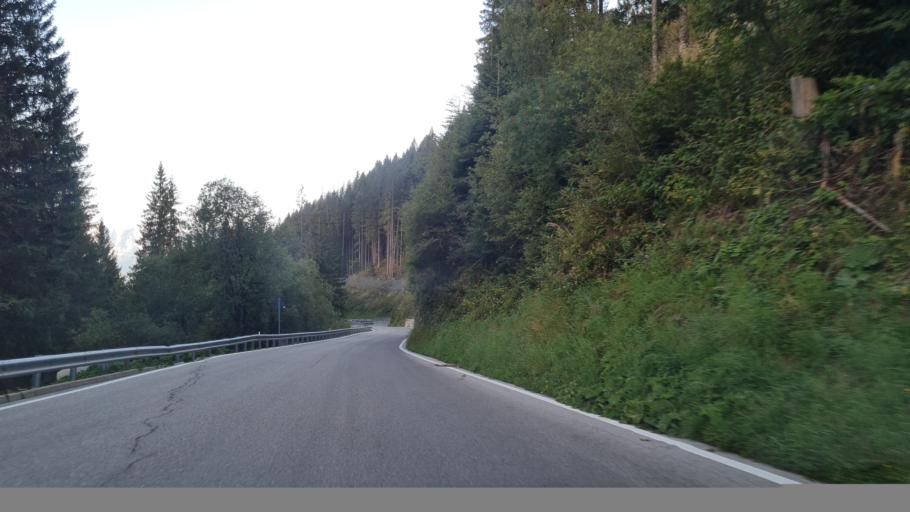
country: IT
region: Trentino-Alto Adige
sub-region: Provincia di Trento
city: Siror
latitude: 46.2513
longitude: 11.8023
